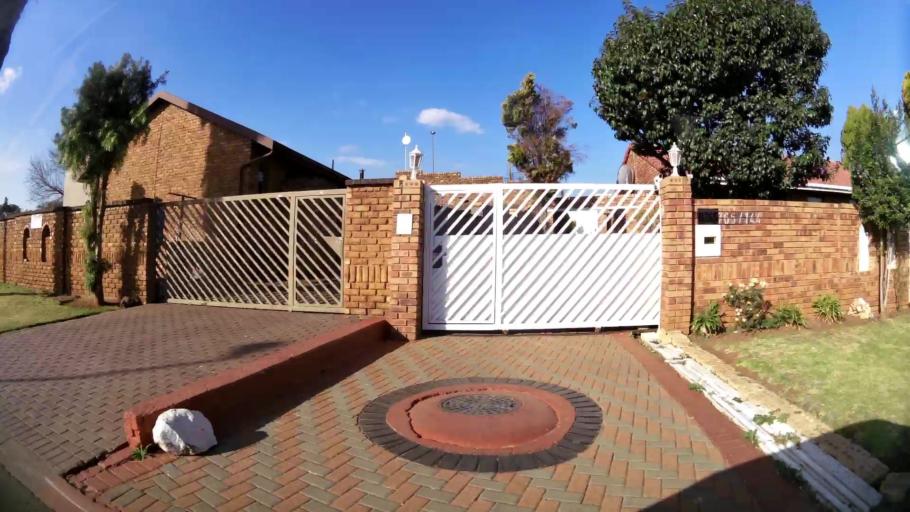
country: ZA
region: Gauteng
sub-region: City of Johannesburg Metropolitan Municipality
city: Soweto
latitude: -26.2648
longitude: 27.9169
